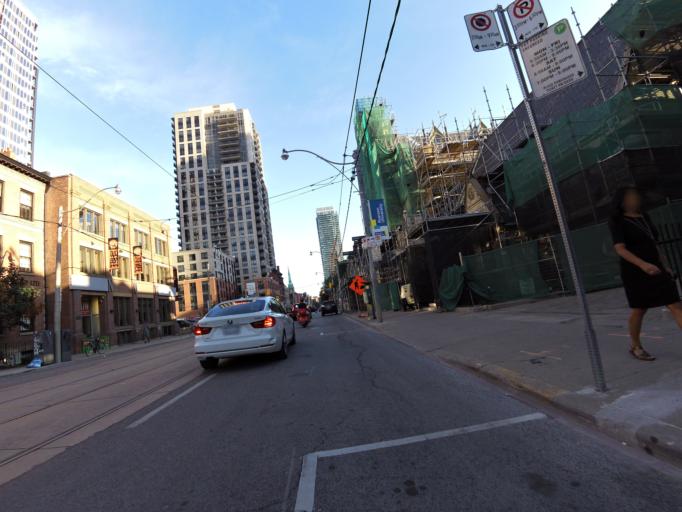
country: CA
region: Ontario
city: Toronto
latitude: 43.6555
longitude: -79.3768
